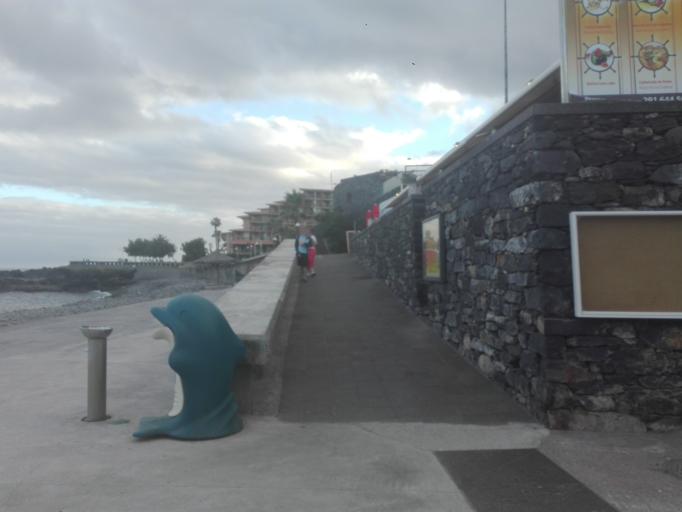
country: PT
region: Madeira
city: Canico
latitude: 32.6475
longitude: -16.8241
